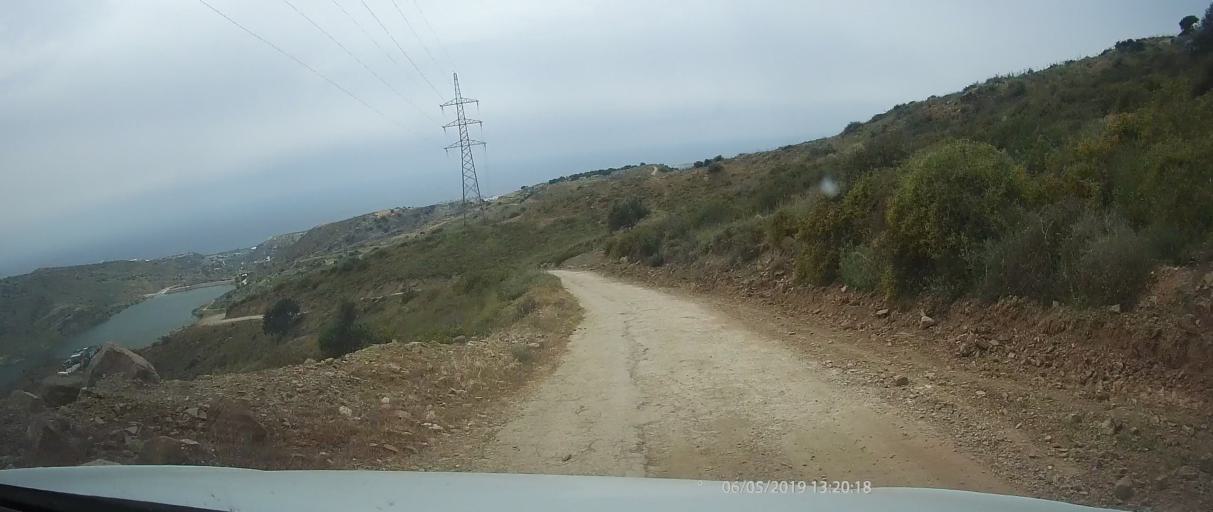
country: CY
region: Pafos
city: Tala
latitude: 34.8650
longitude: 32.4167
